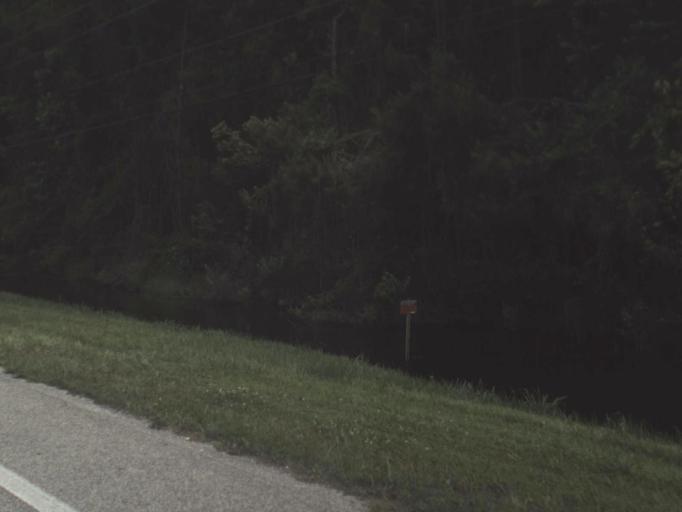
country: US
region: Florida
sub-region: Saint Johns County
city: Palm Valley
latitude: 30.1091
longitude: -81.4833
